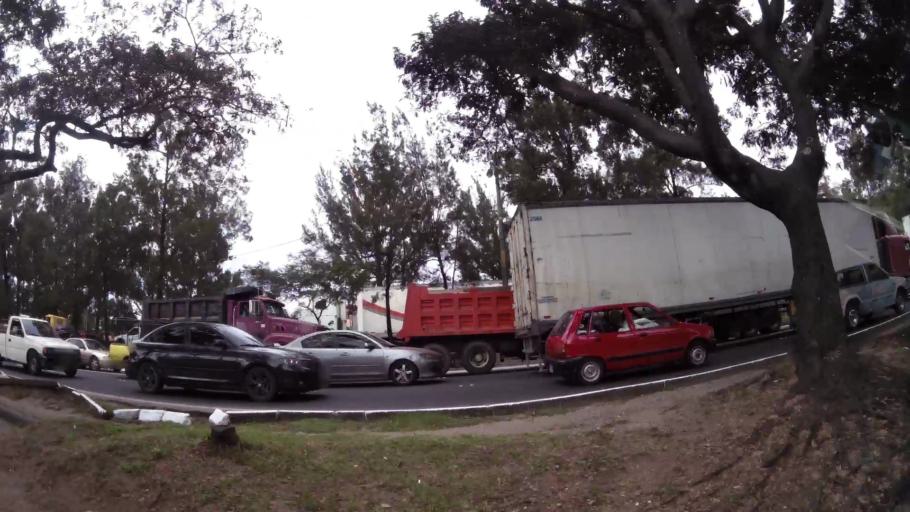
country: GT
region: Guatemala
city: Guatemala City
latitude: 14.6337
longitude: -90.5529
